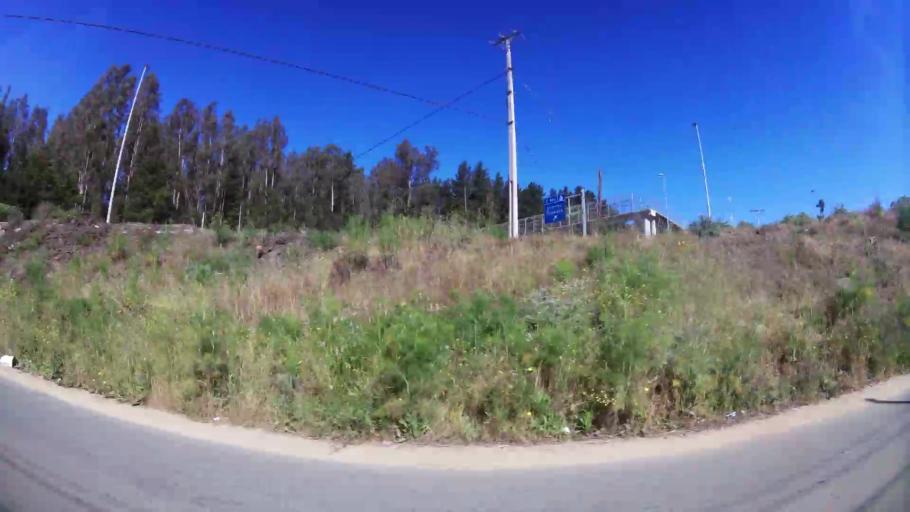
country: CL
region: Valparaiso
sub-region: Provincia de Valparaiso
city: Vina del Mar
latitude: -33.1460
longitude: -71.5607
